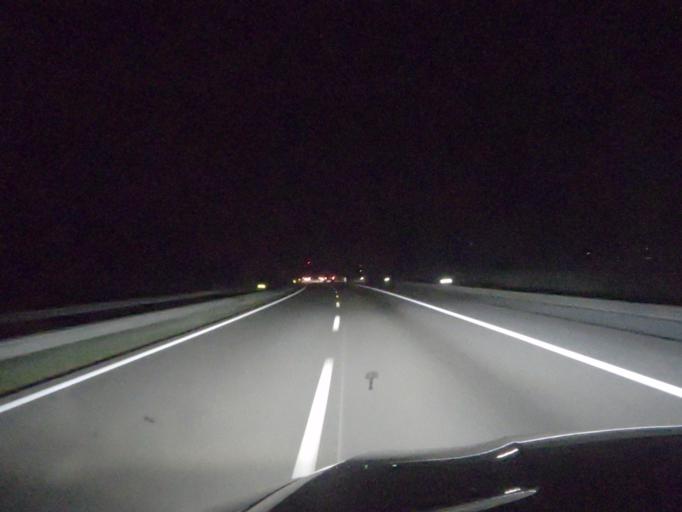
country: PT
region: Aveiro
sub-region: Mealhada
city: Mealhada
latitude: 40.4083
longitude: -8.4919
